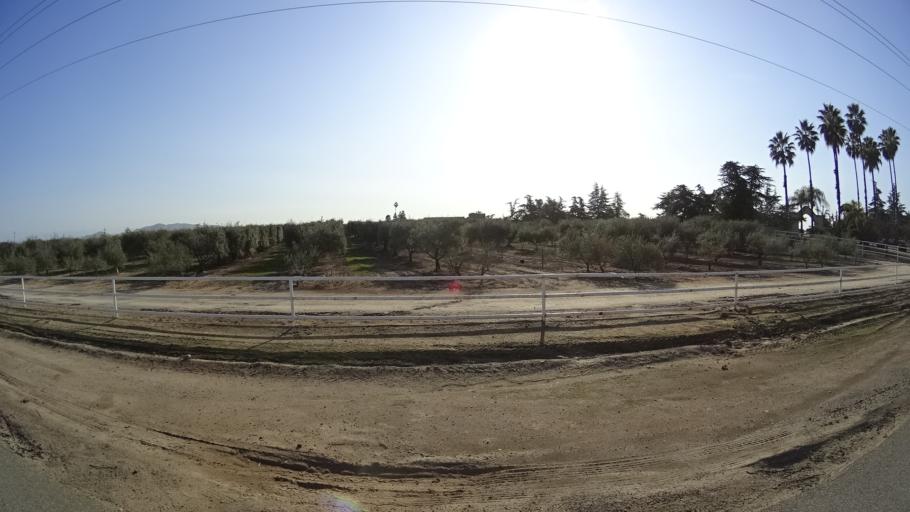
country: US
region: California
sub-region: Fresno County
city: Clovis
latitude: 36.9060
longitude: -119.7322
